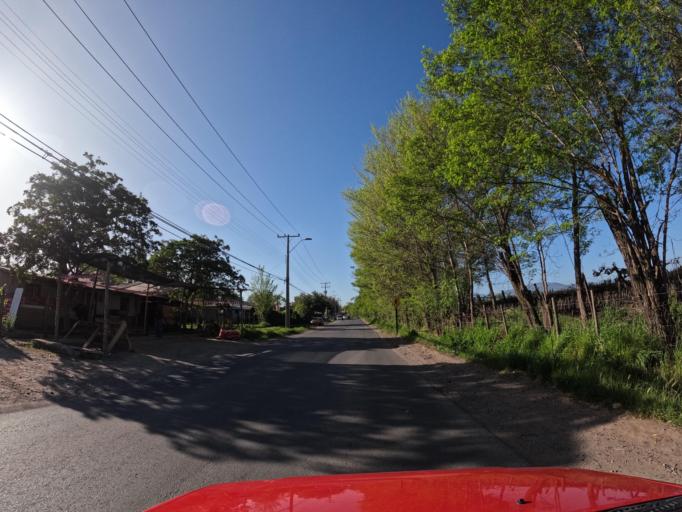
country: CL
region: O'Higgins
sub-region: Provincia de Colchagua
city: Santa Cruz
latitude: -34.7173
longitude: -71.2878
